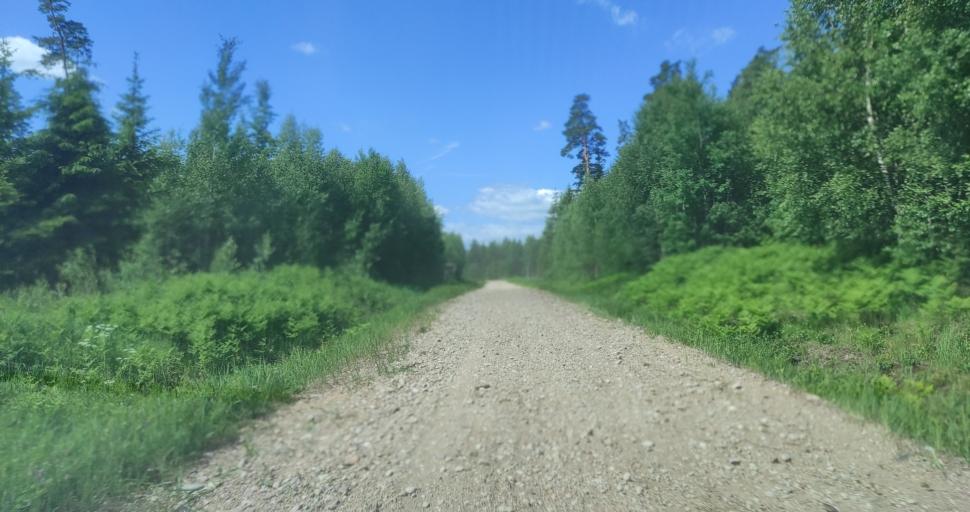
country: LV
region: Alsunga
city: Alsunga
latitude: 56.8891
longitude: 21.7349
